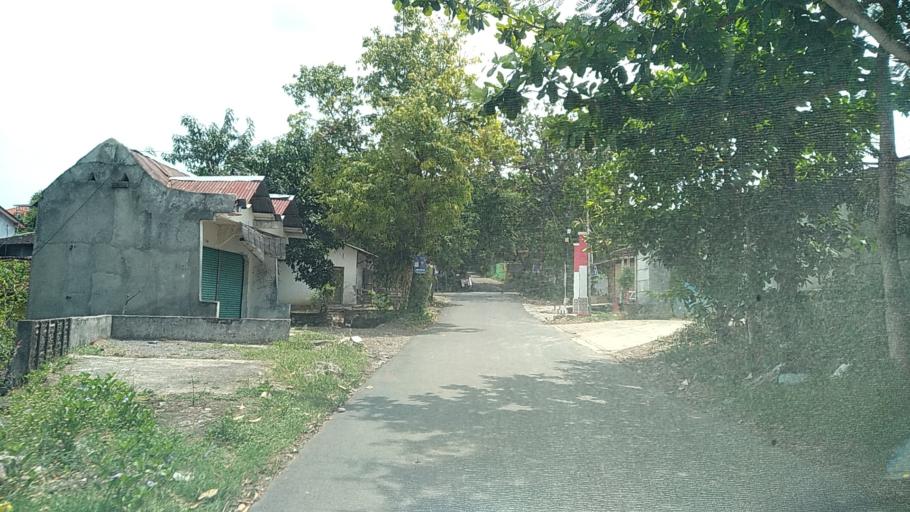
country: ID
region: Central Java
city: Semarang
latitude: -6.9917
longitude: 110.3967
